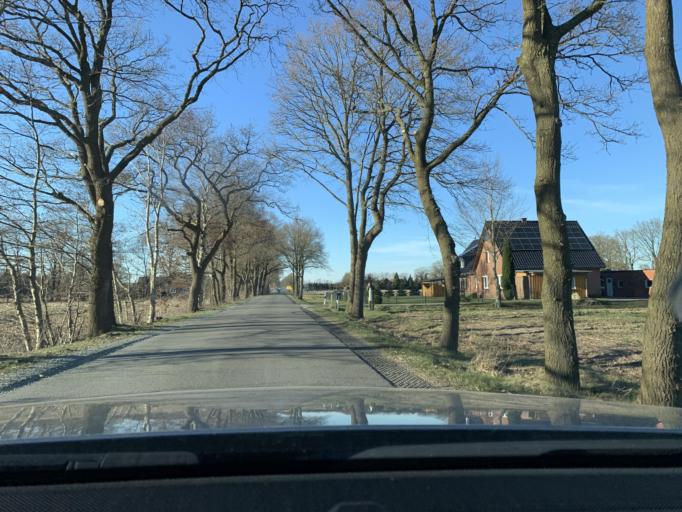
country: DE
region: Lower Saxony
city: Wardenburg
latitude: 53.0602
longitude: 8.2862
